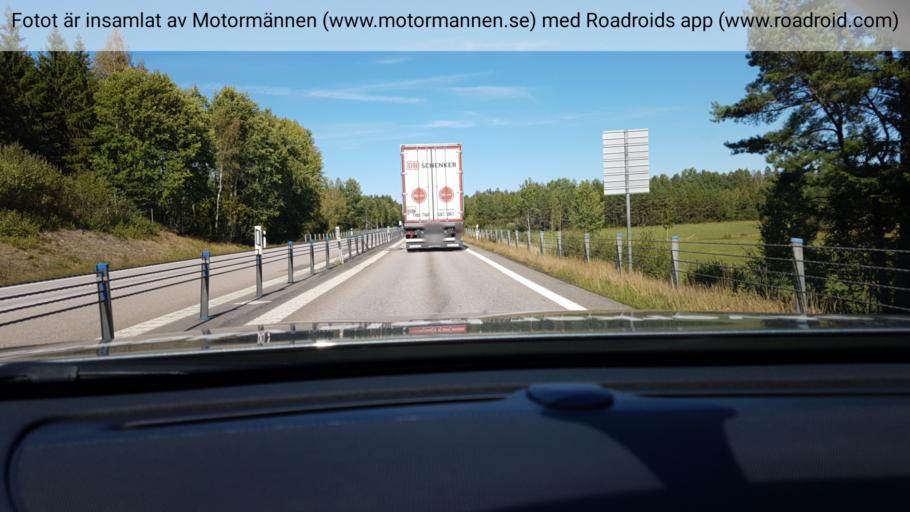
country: SE
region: Vaestra Goetaland
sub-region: Mariestads Kommun
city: Mariestad
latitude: 58.6350
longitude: 13.8152
